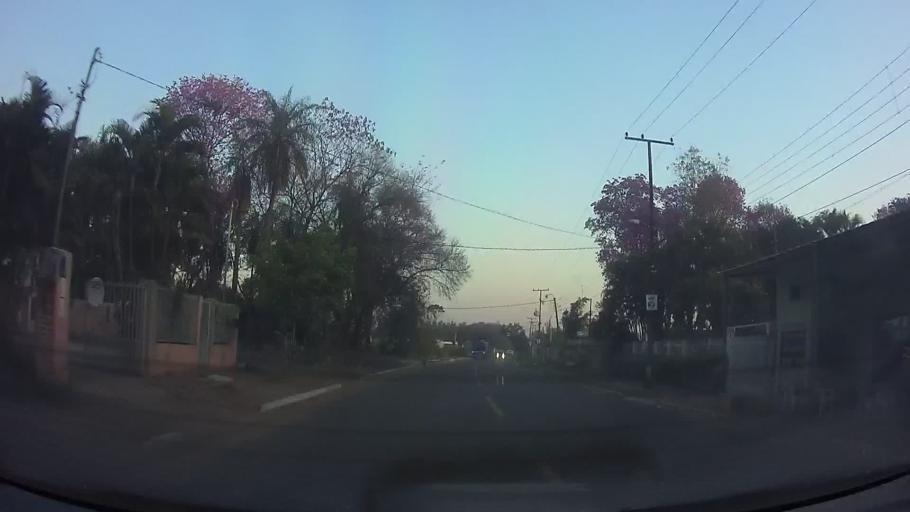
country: PY
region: Central
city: Limpio
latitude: -25.2403
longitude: -57.4909
